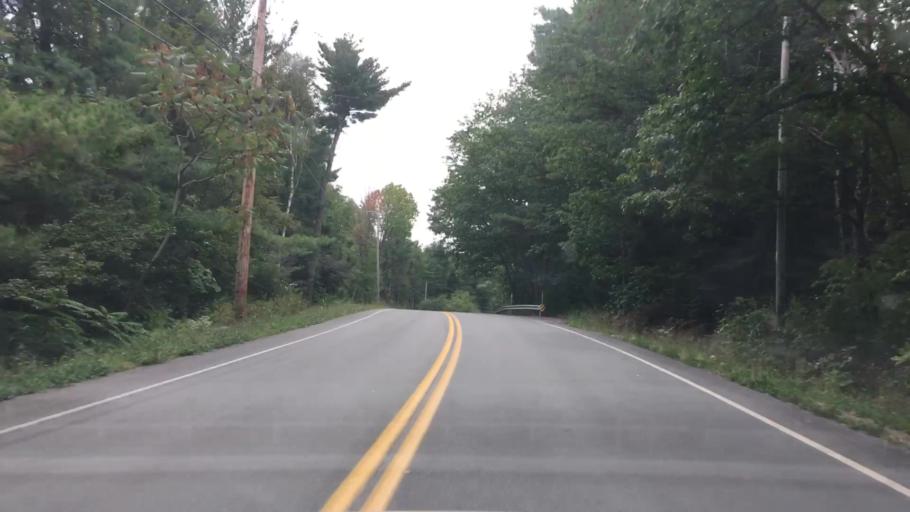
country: US
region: Maine
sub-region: Penobscot County
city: Milford
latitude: 44.9564
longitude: -68.6981
